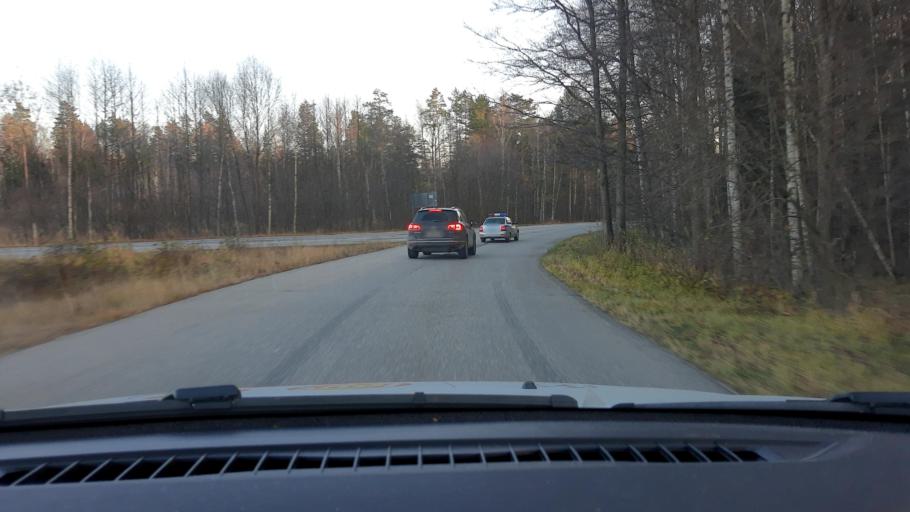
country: RU
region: Nizjnij Novgorod
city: Volodarsk
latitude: 56.2843
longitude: 43.1652
